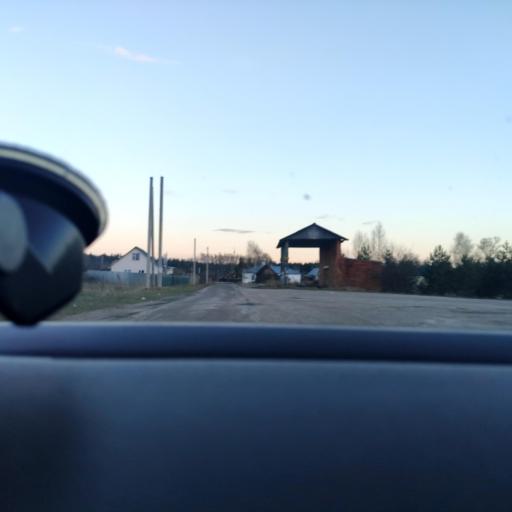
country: RU
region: Moskovskaya
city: Shaturtorf
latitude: 55.4357
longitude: 39.4269
